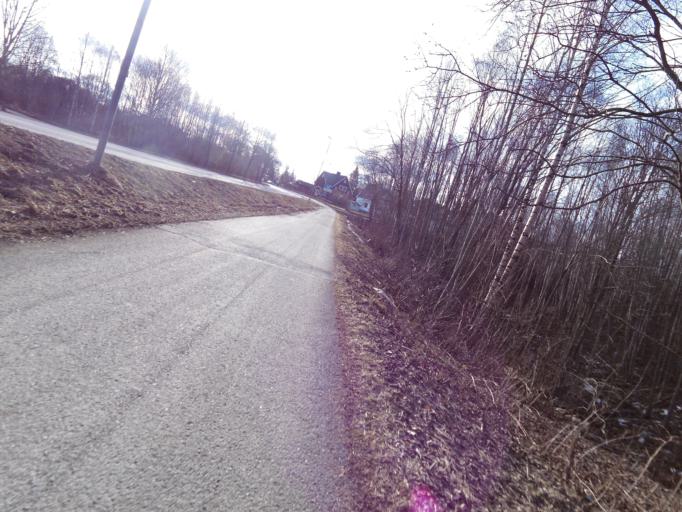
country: SE
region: Gaevleborg
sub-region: Gavle Kommun
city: Gavle
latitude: 60.6818
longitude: 17.1208
